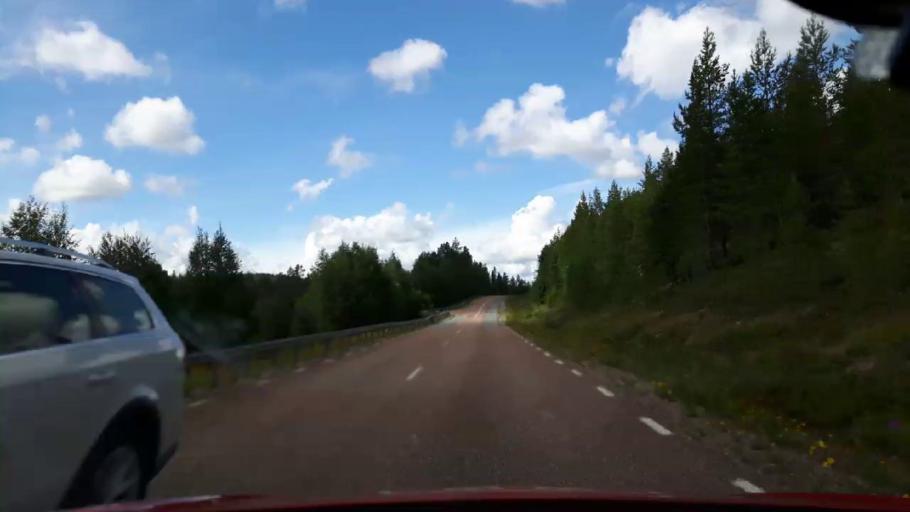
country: SE
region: Dalarna
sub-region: Alvdalens Kommun
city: AElvdalen
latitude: 61.7981
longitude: 13.6891
